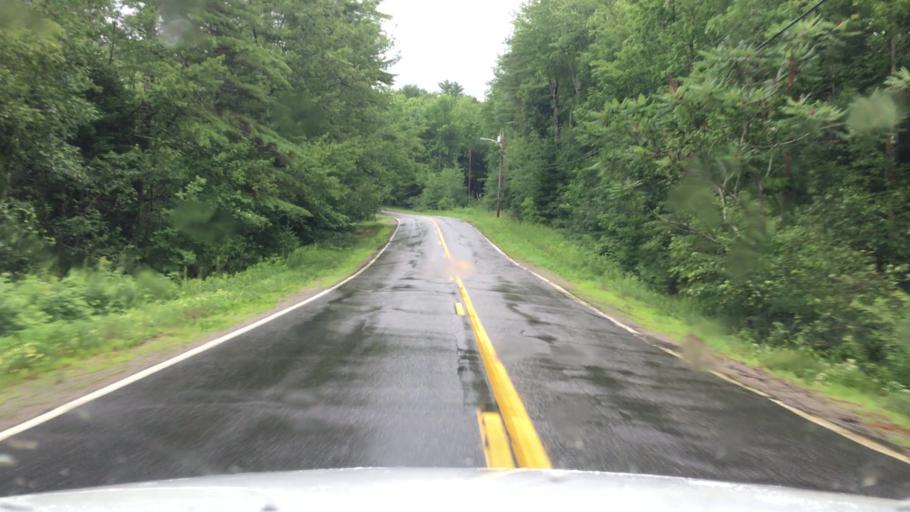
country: US
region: Maine
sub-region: Kennebec County
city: Winthrop
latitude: 44.2814
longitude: -69.9323
